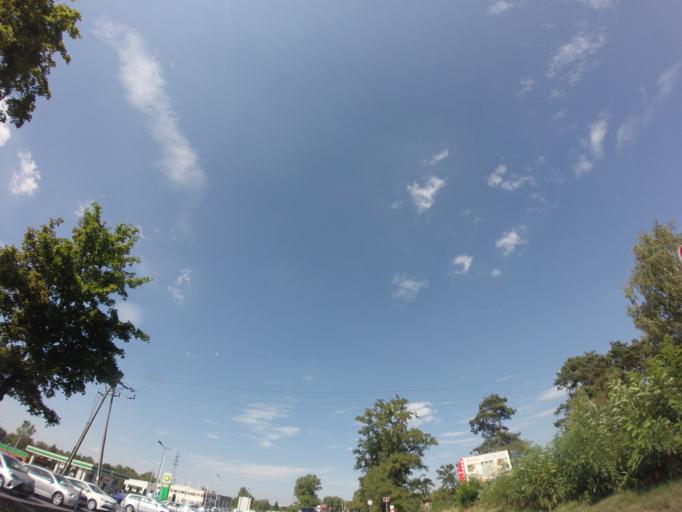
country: PL
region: Lower Silesian Voivodeship
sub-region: Powiat lubinski
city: Lubin
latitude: 51.3757
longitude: 16.1903
